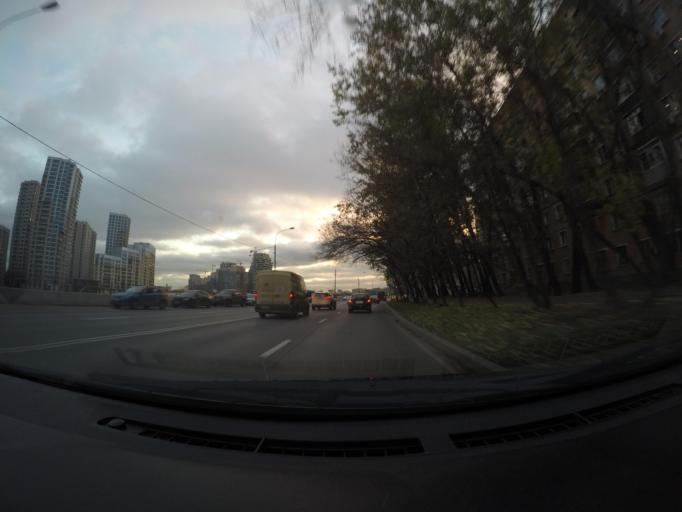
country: RU
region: Moscow
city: Taganskiy
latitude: 55.7213
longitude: 37.6547
